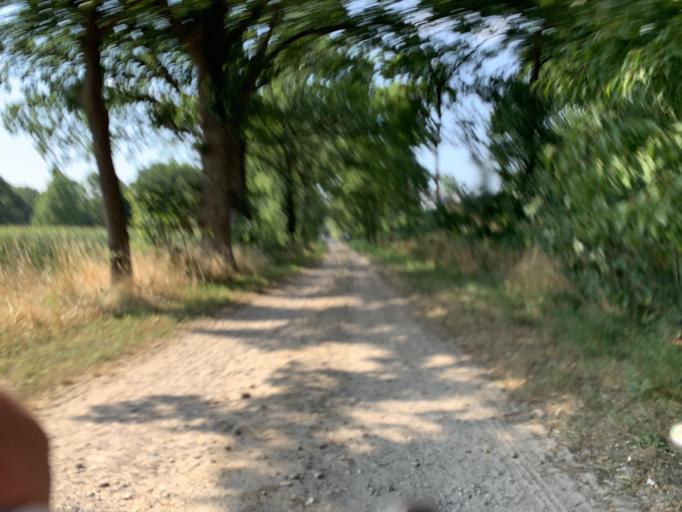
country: DE
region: Lower Saxony
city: Thomasburg
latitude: 53.2353
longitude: 10.6348
